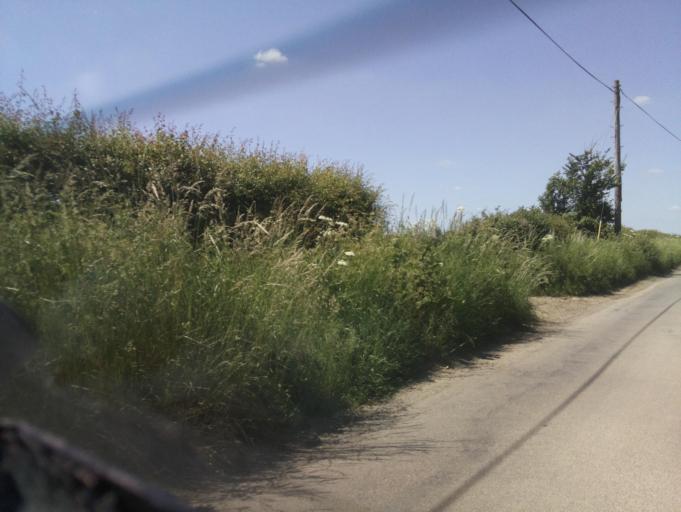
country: GB
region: England
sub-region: Wiltshire
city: Bremhill
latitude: 51.4614
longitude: -2.0676
